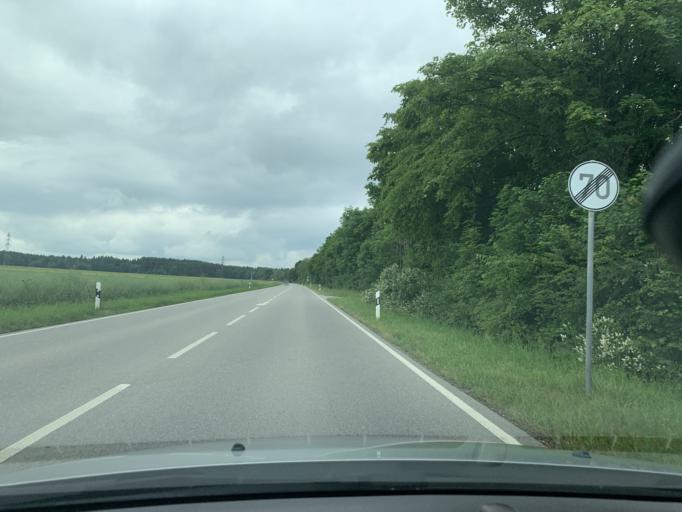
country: DE
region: Bavaria
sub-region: Upper Bavaria
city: Sauerlach
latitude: 47.9375
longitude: 11.6523
